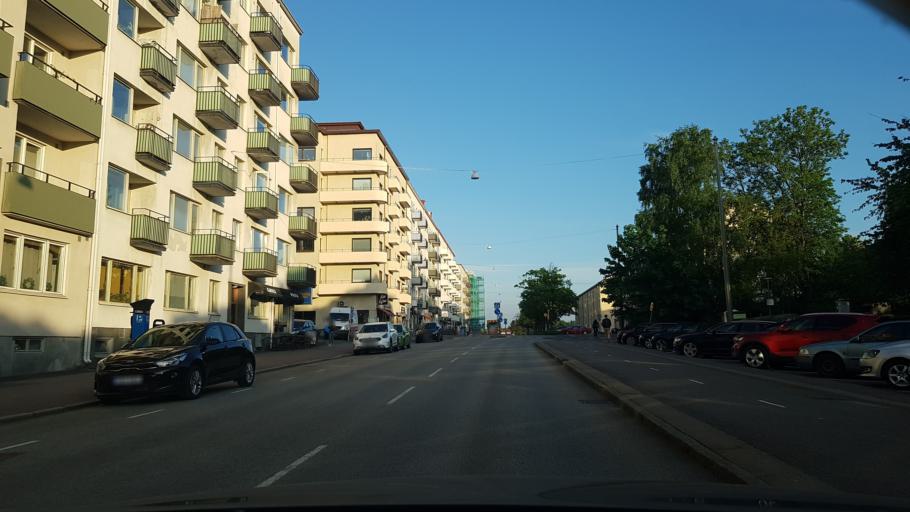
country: SE
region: Vaestra Goetaland
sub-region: Goteborg
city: Goeteborg
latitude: 57.6882
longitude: 11.9818
